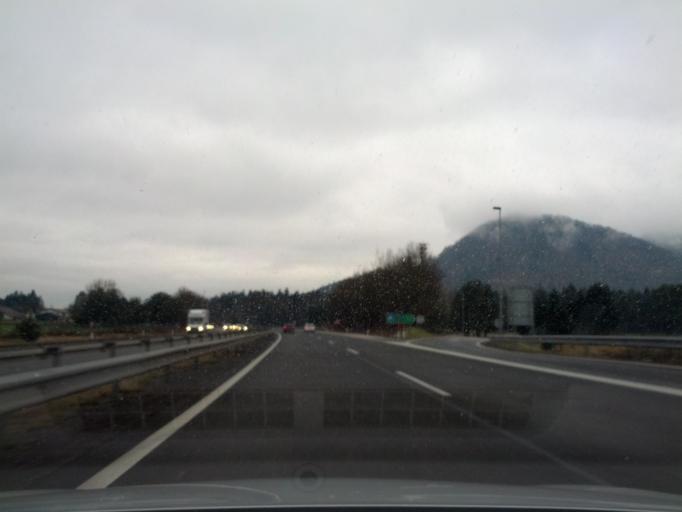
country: SI
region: Medvode
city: Zgornje Pirnice
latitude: 46.1472
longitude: 14.4761
